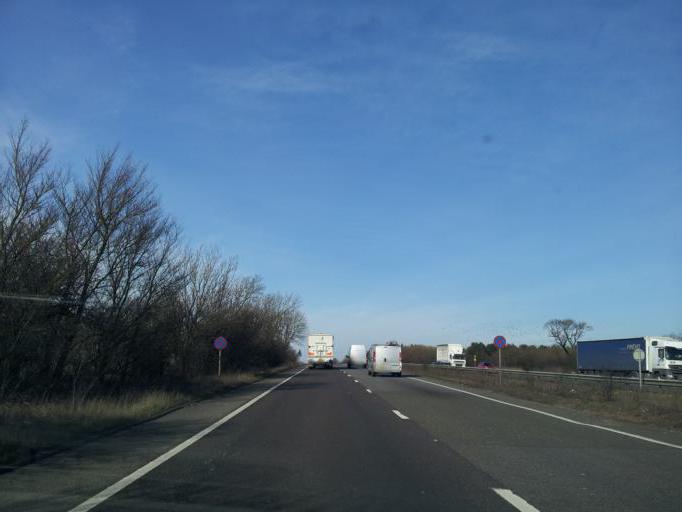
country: GB
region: England
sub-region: District of Rutland
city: Greetham
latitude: 52.7478
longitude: -0.6048
